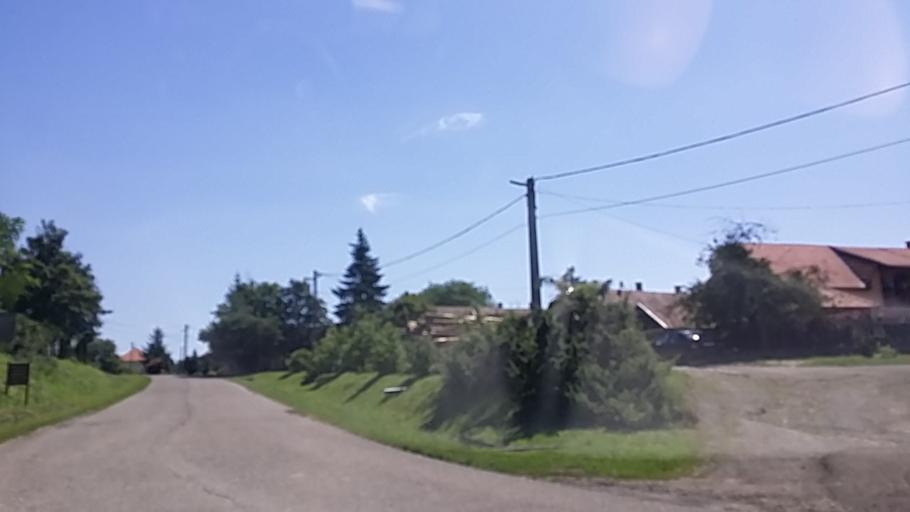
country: HU
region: Pest
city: Szob
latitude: 47.8638
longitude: 18.8727
